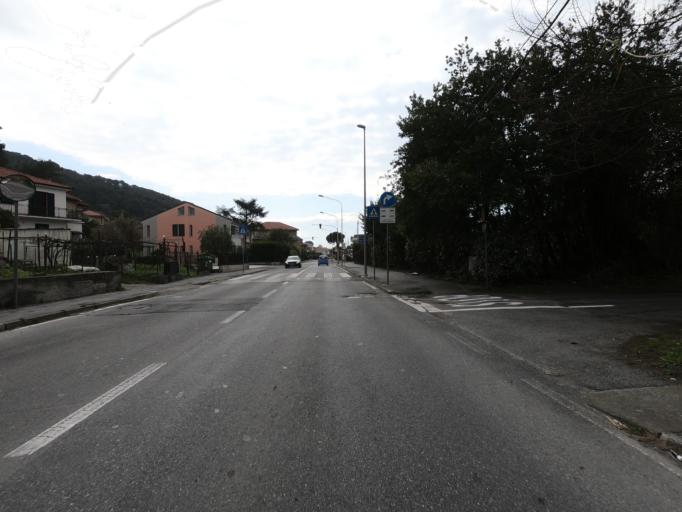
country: IT
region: Liguria
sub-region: Provincia di Savona
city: Andora
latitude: 43.9615
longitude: 8.1432
